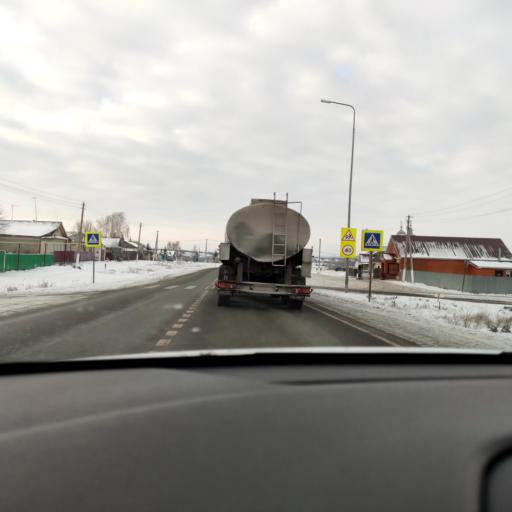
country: RU
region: Tatarstan
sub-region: Arskiy Rayon
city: Arsk
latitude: 56.0261
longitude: 49.7318
